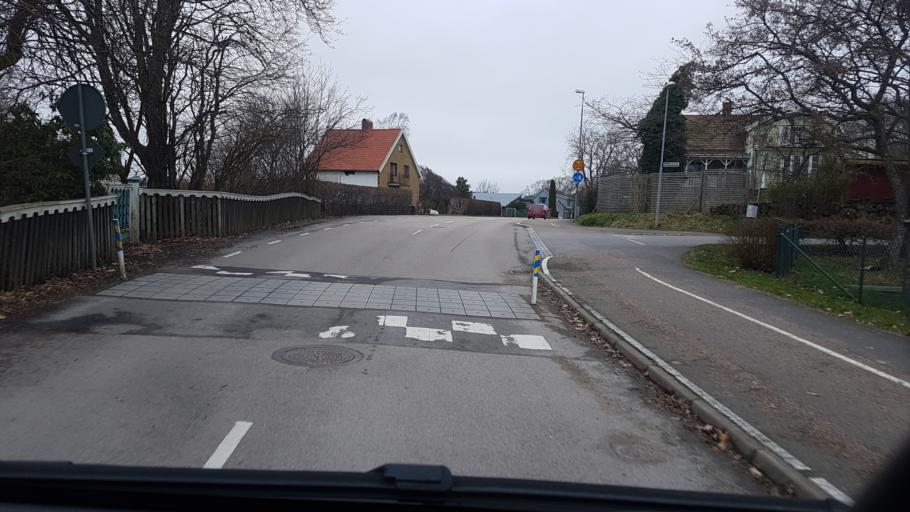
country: SE
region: Vaestra Goetaland
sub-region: Lerums Kommun
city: Lerum
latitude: 57.7714
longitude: 12.2478
